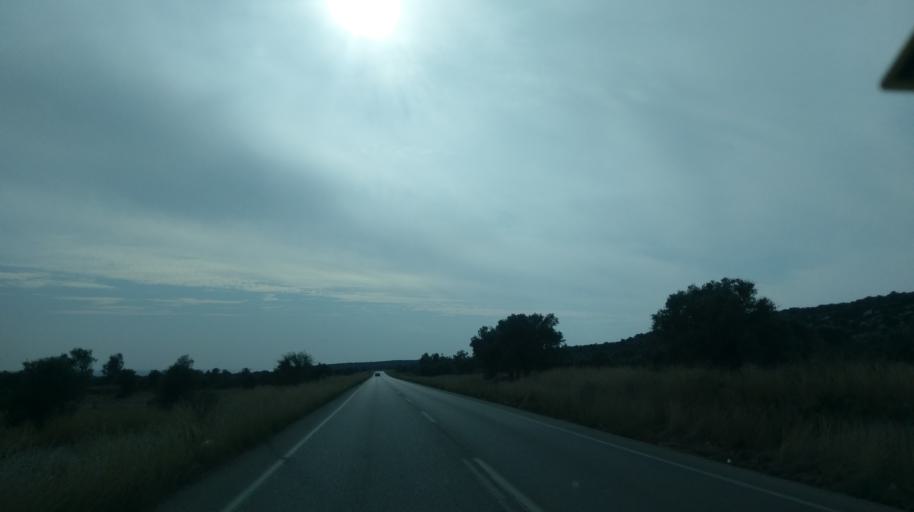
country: CY
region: Ammochostos
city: Leonarisso
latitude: 35.4079
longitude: 34.1094
